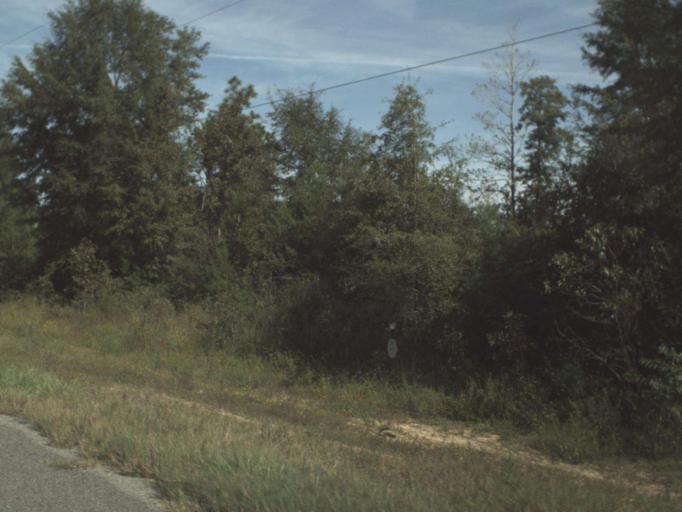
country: US
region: Florida
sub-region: Washington County
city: Chipley
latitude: 30.5913
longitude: -85.5920
